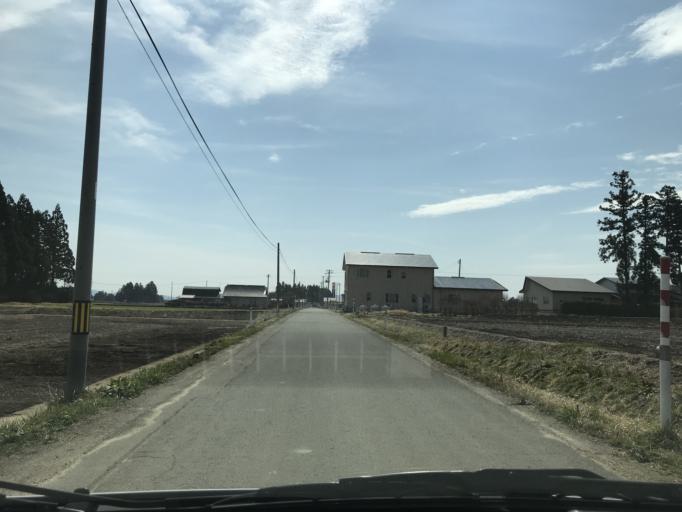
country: JP
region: Iwate
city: Mizusawa
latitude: 39.1404
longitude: 141.0438
